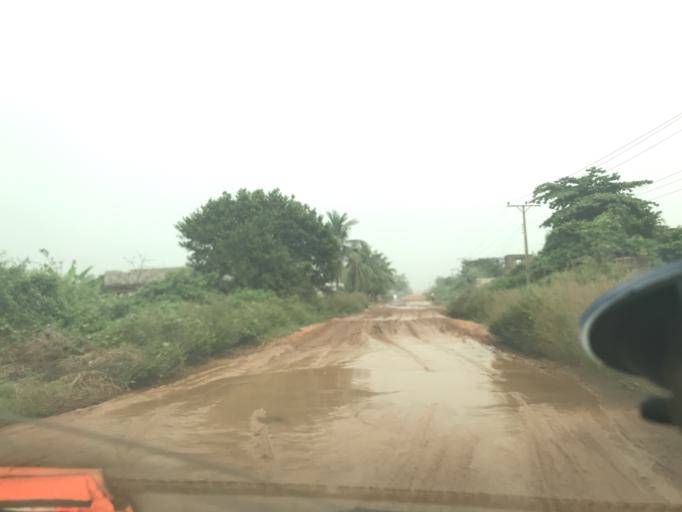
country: NG
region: Ogun
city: Ado Odo
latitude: 6.5459
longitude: 2.9485
